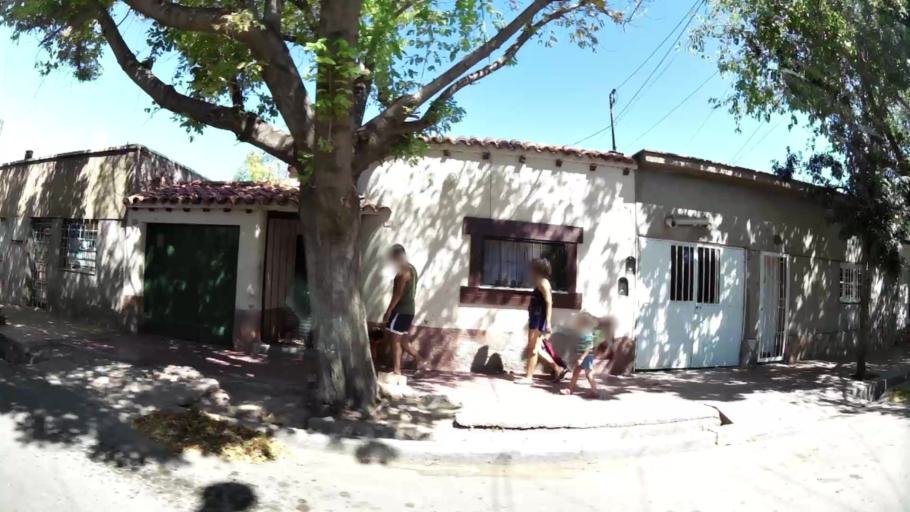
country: AR
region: Mendoza
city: Las Heras
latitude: -32.8527
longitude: -68.8356
